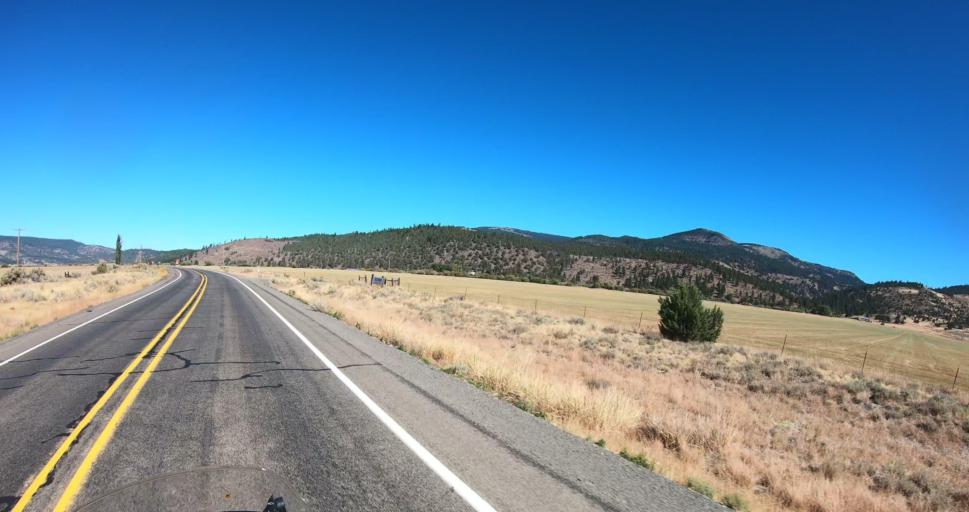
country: US
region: Oregon
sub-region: Lake County
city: Lakeview
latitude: 42.3331
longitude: -120.2987
